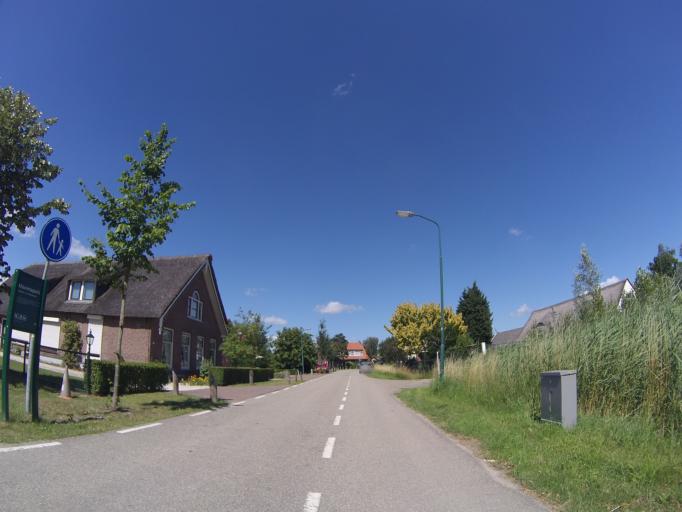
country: NL
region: Utrecht
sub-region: Stichtse Vecht
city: Spechtenkamp
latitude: 52.0960
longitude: 5.0263
